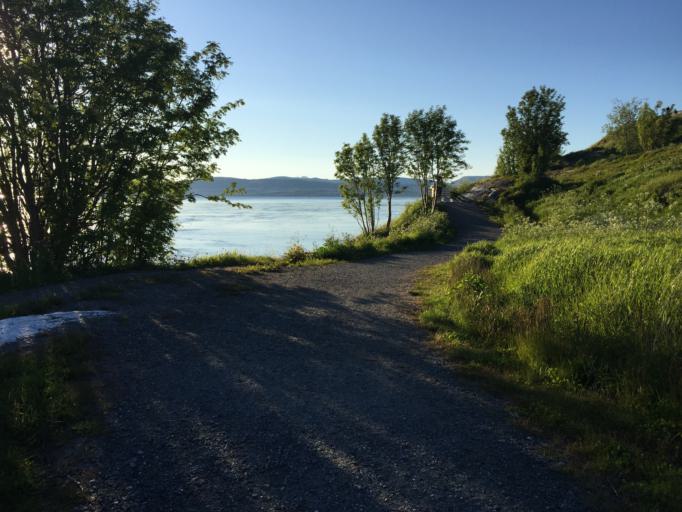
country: NO
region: Nordland
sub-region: Bodo
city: Loding
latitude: 67.2345
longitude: 14.6146
